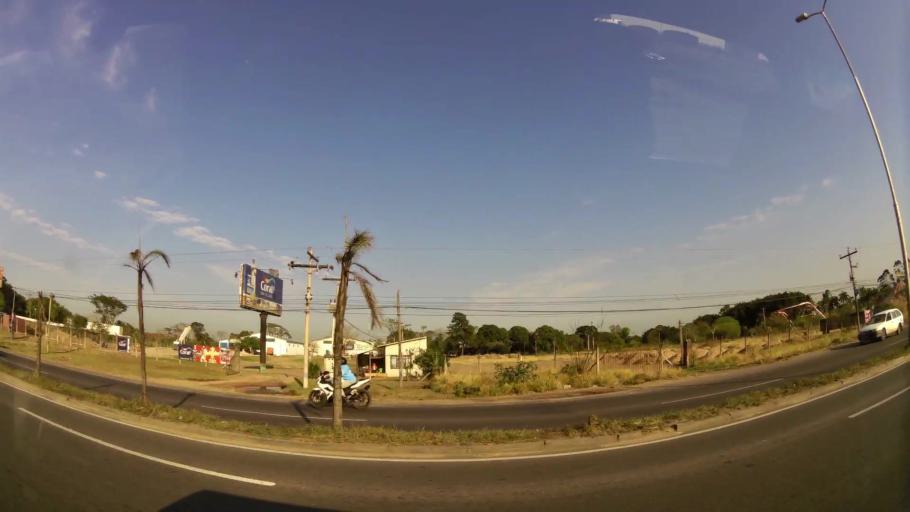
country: BO
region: Santa Cruz
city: Santa Cruz de la Sierra
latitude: -17.6761
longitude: -63.1586
